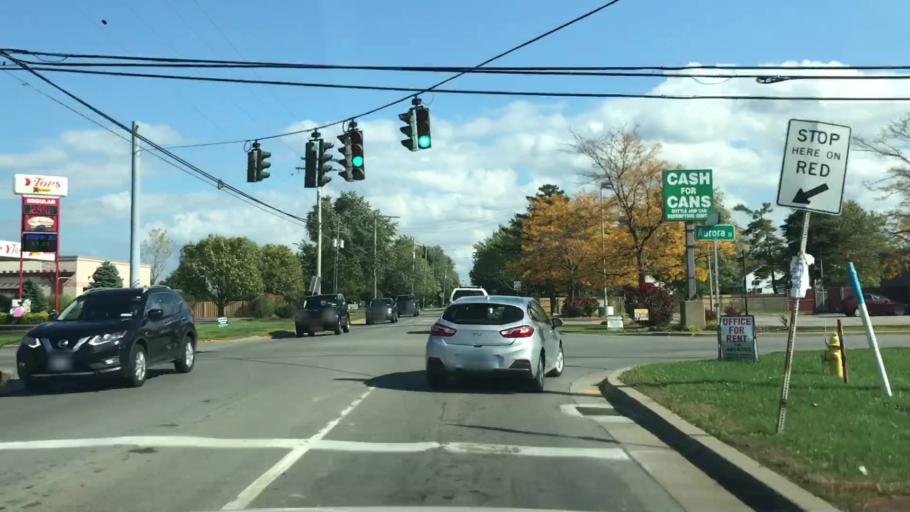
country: US
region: New York
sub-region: Erie County
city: Lancaster
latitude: 42.8807
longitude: -78.6770
